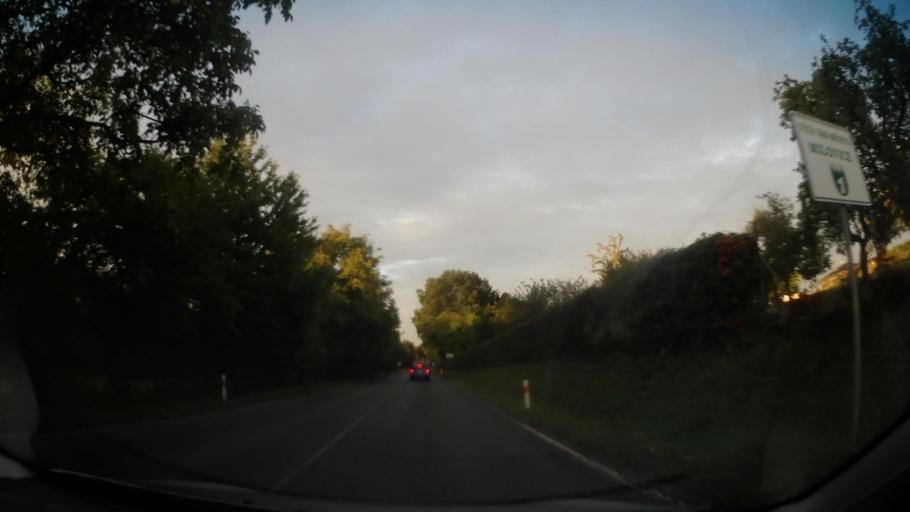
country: CZ
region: Central Bohemia
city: Milovice
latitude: 50.2240
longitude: 14.8791
